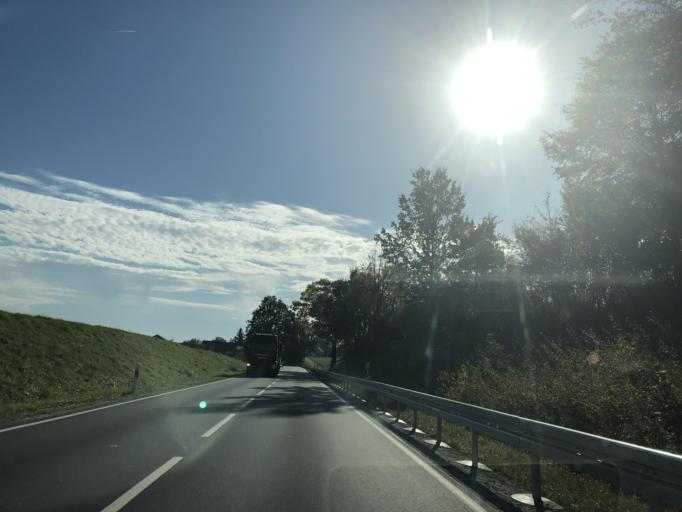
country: DE
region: Bavaria
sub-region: Lower Bavaria
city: Grafling
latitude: 48.8711
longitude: 12.9590
